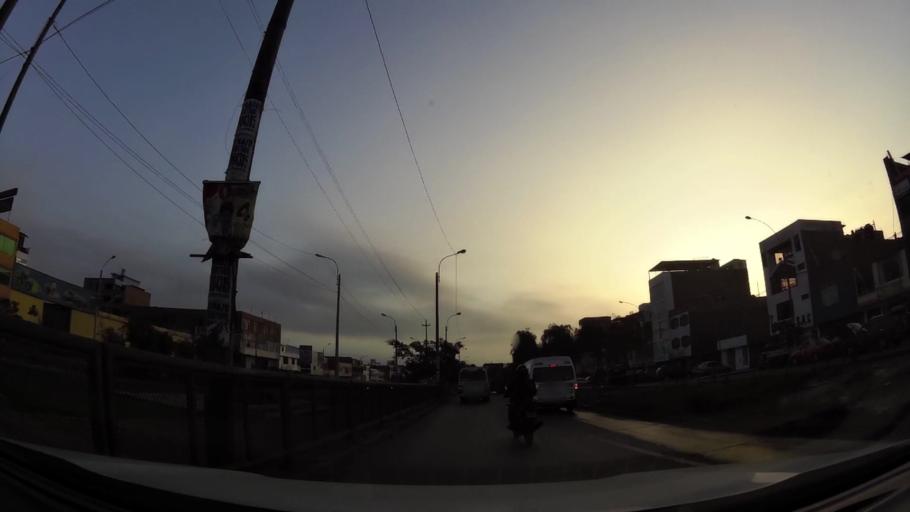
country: PE
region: Lima
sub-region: Lima
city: Independencia
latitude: -12.0114
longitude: -77.0724
